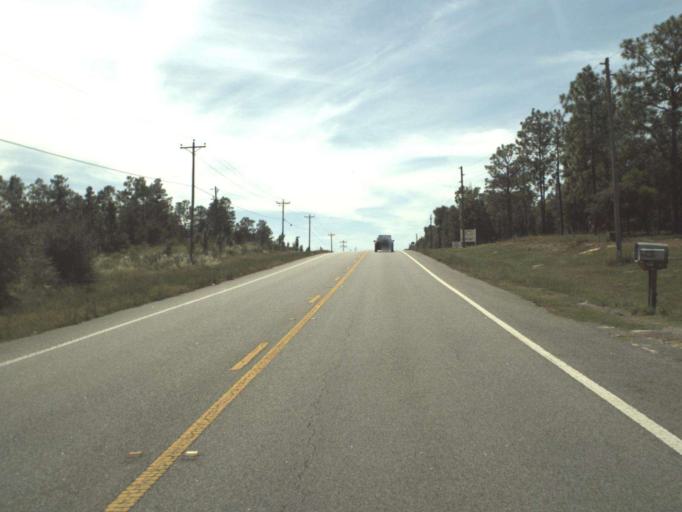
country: US
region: Florida
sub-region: Bay County
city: Youngstown
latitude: 30.5273
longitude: -85.6465
